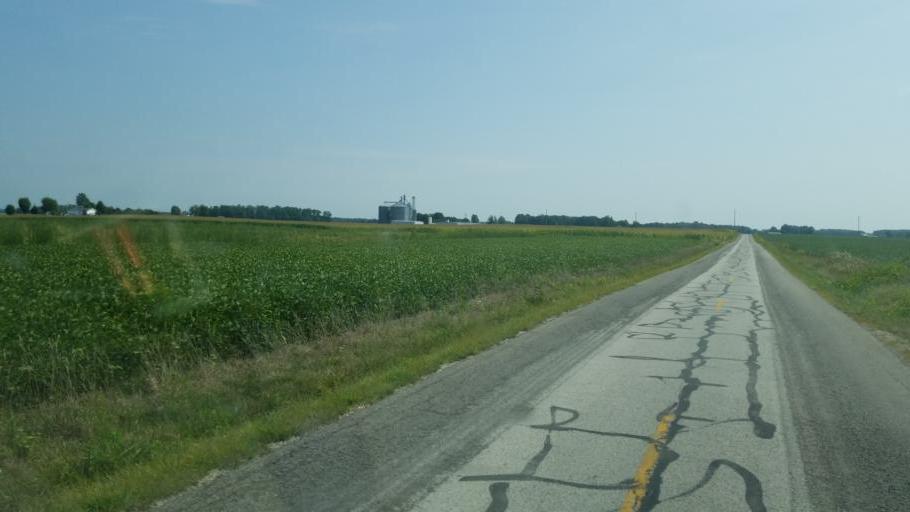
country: US
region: Ohio
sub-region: Crawford County
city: Crestline
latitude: 40.8412
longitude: -82.7444
